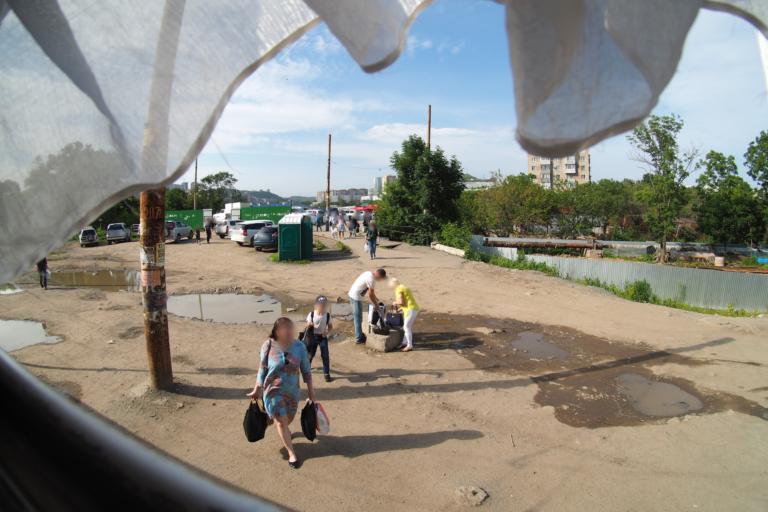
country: RU
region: Primorskiy
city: Vladivostok
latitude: 43.1028
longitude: 131.9405
